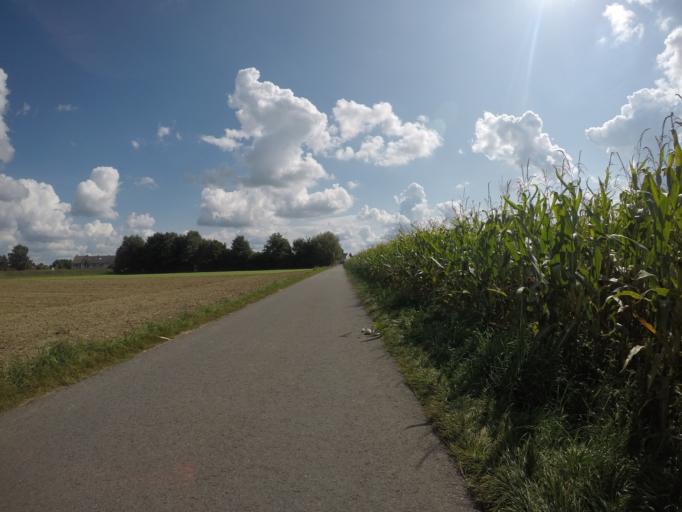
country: DE
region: North Rhine-Westphalia
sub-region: Regierungsbezirk Dusseldorf
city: Hamminkeln
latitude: 51.7365
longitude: 6.5858
